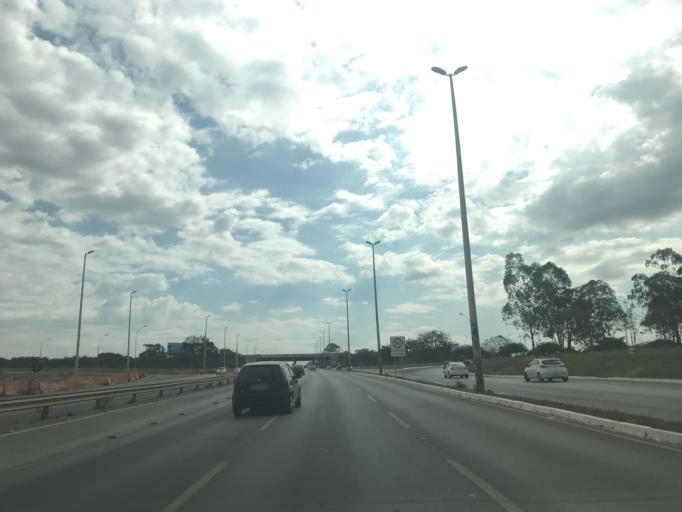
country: BR
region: Federal District
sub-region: Brasilia
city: Brasilia
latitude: -15.8491
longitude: -47.9317
